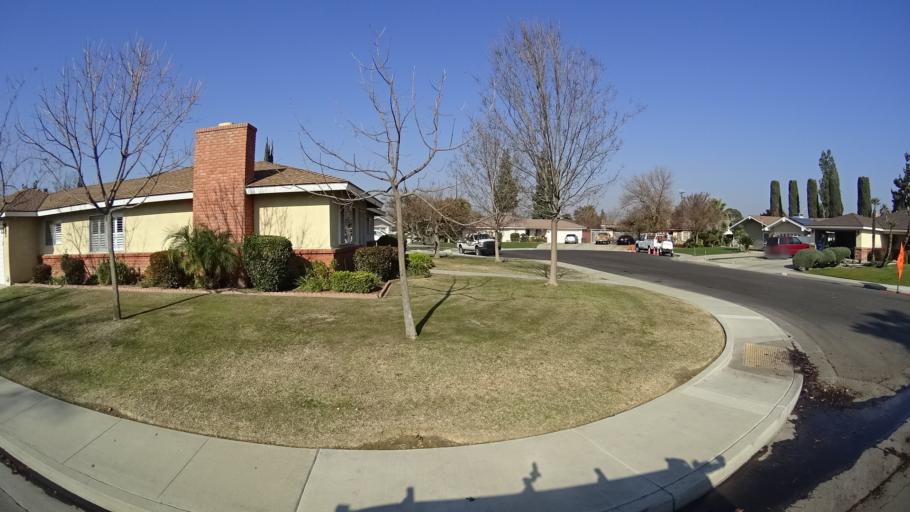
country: US
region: California
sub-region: Kern County
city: Greenacres
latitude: 35.3533
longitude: -119.0682
